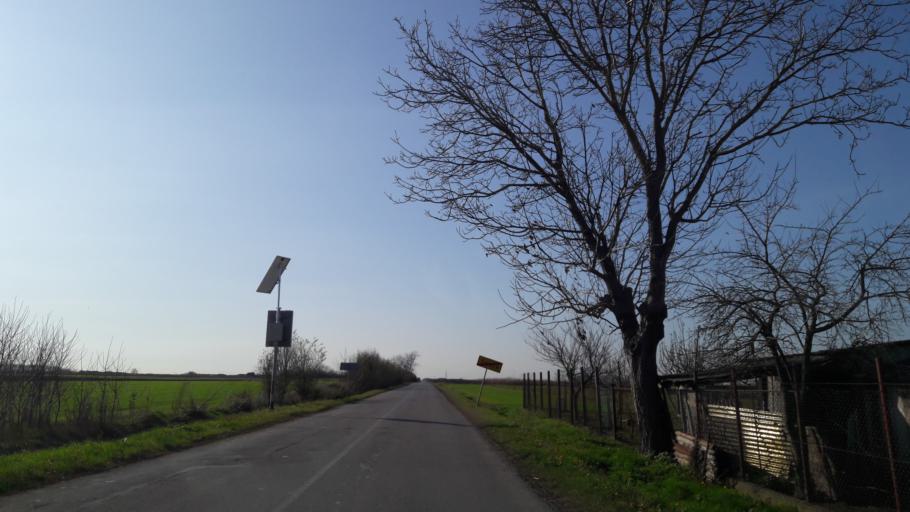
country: HR
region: Osjecko-Baranjska
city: Tenja
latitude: 45.4927
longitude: 18.7367
